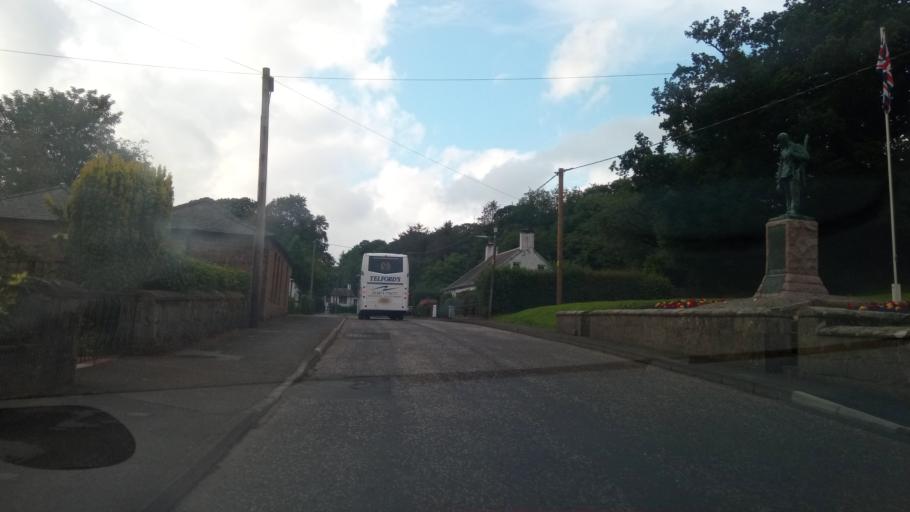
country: GB
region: Scotland
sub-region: Dumfries and Galloway
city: Langholm
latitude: 55.0780
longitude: -2.9534
